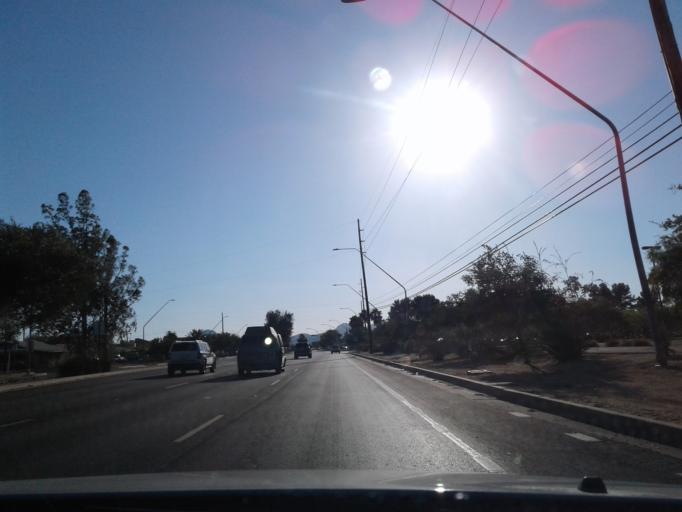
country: US
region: Arizona
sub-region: Pima County
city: Tucson
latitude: 32.2071
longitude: -110.9235
